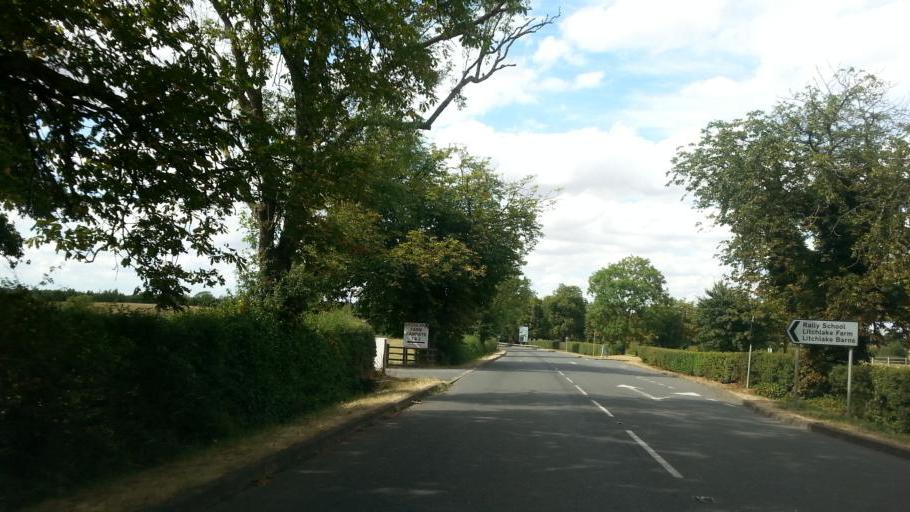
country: GB
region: England
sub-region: Northamptonshire
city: Silverstone
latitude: 52.0780
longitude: -1.0264
